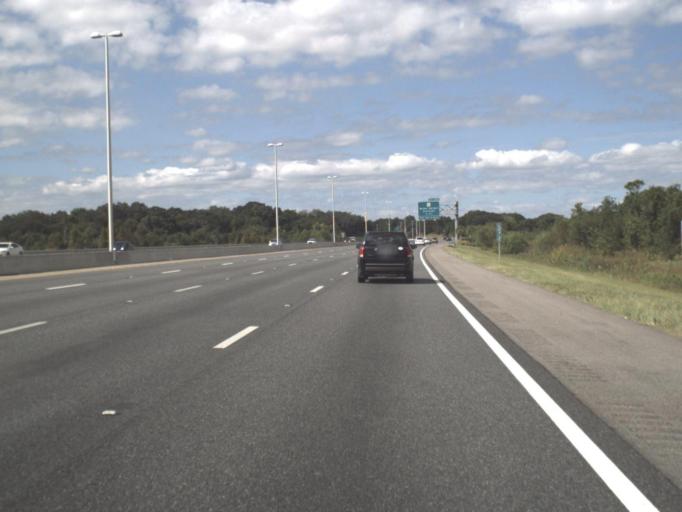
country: US
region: Florida
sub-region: Orange County
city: Oakland
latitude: 28.5464
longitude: -81.6190
